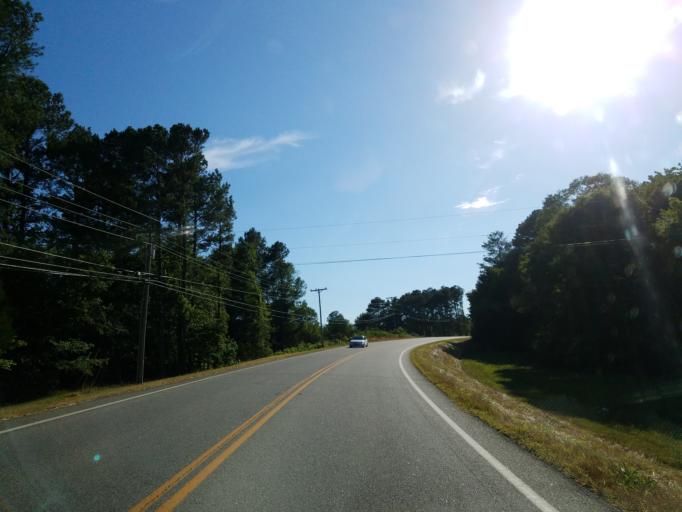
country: US
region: Georgia
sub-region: Gordon County
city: Calhoun
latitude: 34.5722
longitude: -84.9707
